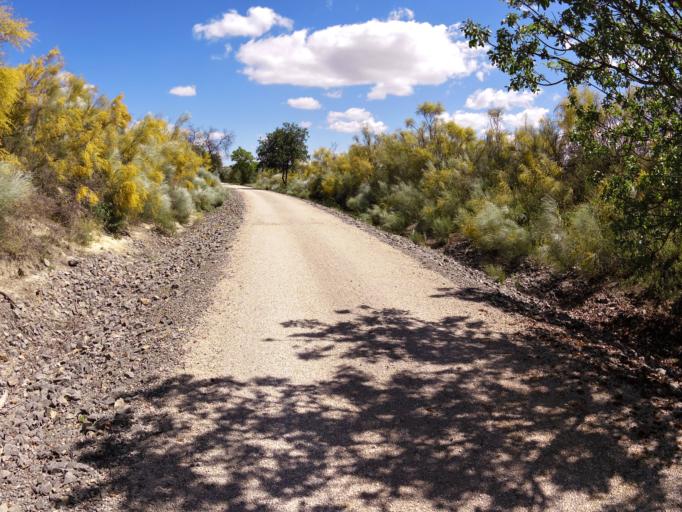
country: ES
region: Andalusia
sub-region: Provincia de Jaen
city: Alcaudete
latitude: 37.6506
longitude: -4.0622
